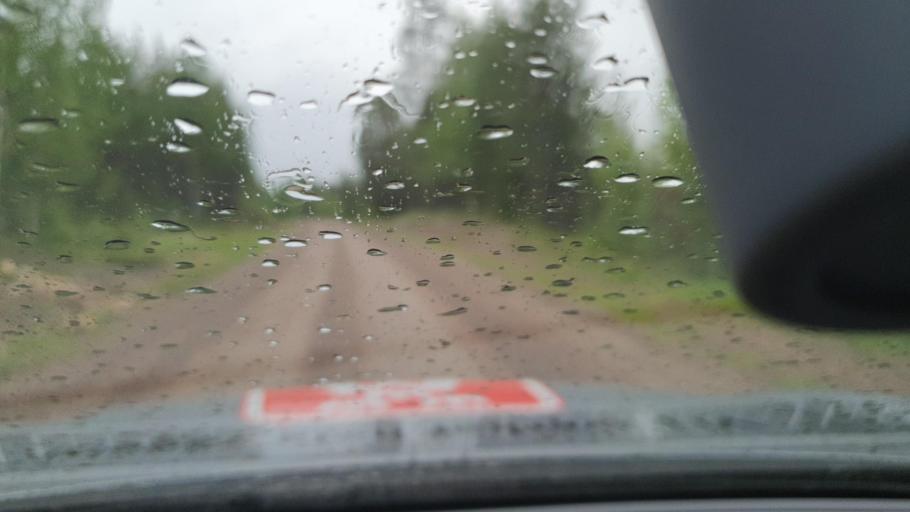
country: SE
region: Norrbotten
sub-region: Overkalix Kommun
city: OEverkalix
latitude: 66.5135
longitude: 22.7489
